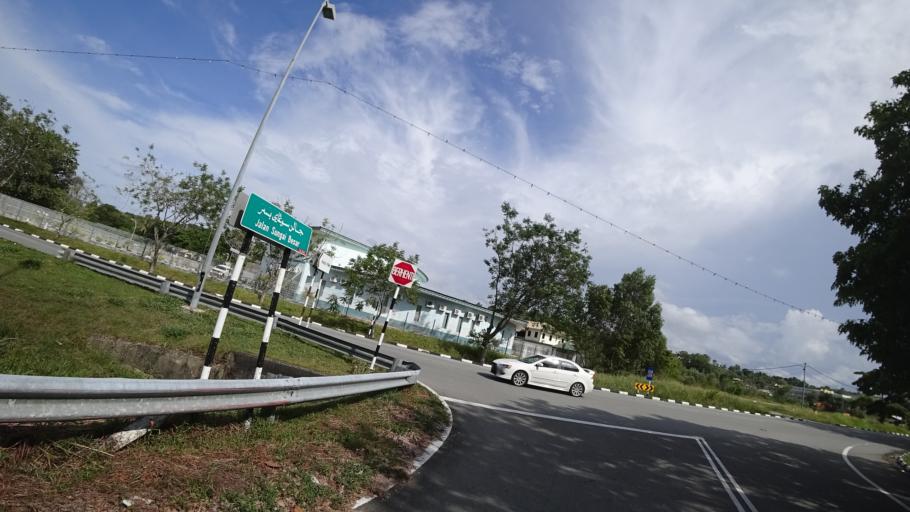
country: BN
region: Tutong
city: Tutong
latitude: 4.8171
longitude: 114.6642
